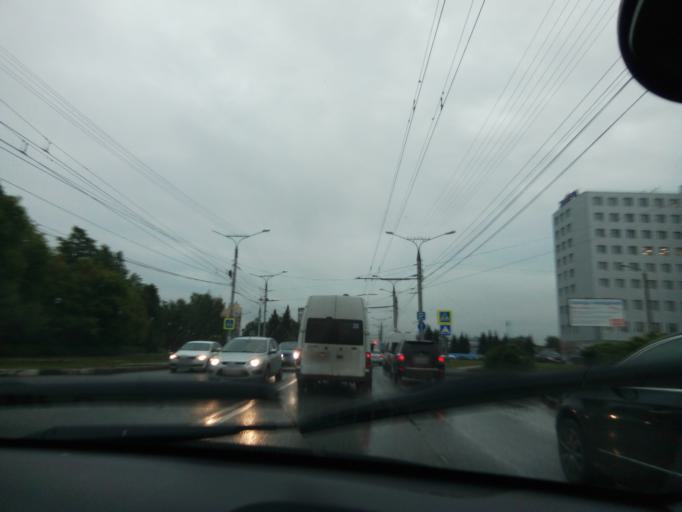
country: RU
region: Chuvashia
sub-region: Cheboksarskiy Rayon
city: Cheboksary
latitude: 56.1450
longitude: 47.2046
